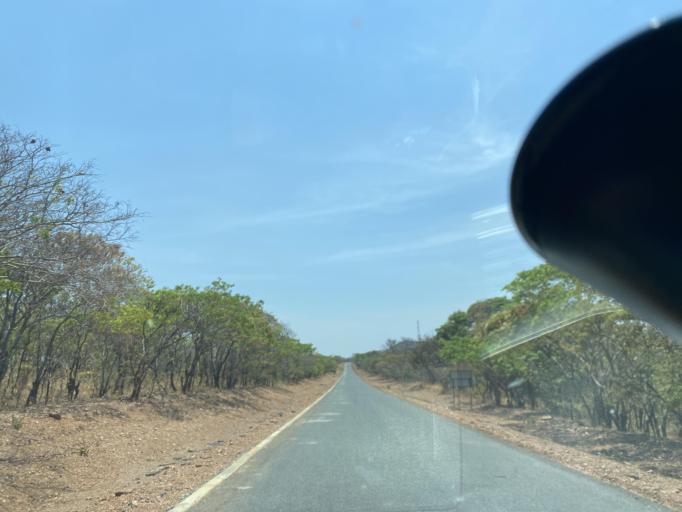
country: ZM
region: Lusaka
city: Kafue
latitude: -15.8490
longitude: 28.4156
